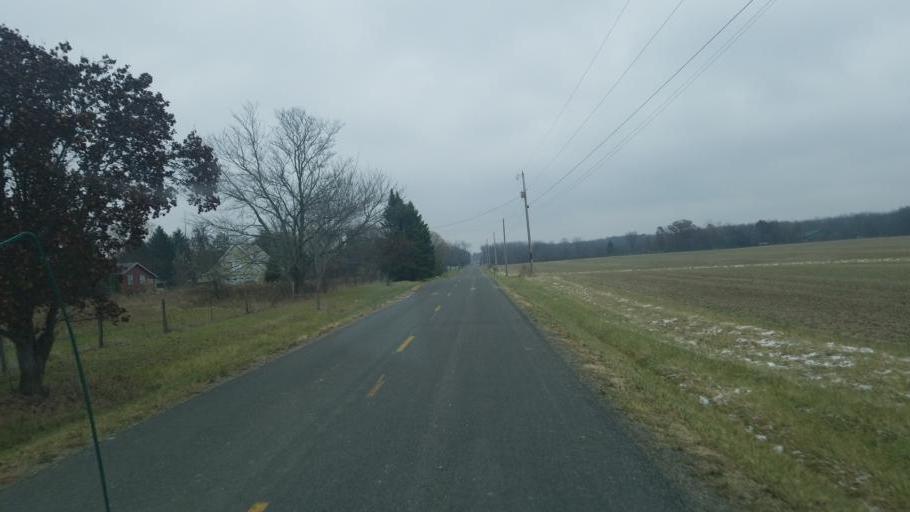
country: US
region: Ohio
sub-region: Medina County
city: Lodi
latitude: 41.1129
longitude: -82.0489
